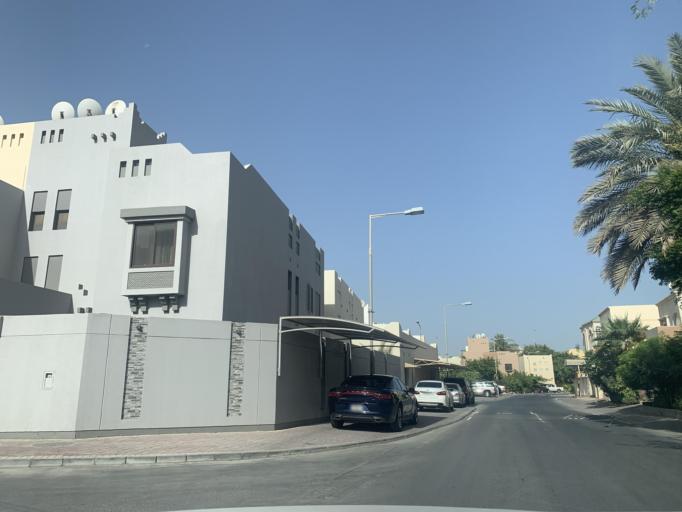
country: BH
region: Manama
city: Jidd Hafs
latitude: 26.2111
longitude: 50.5642
